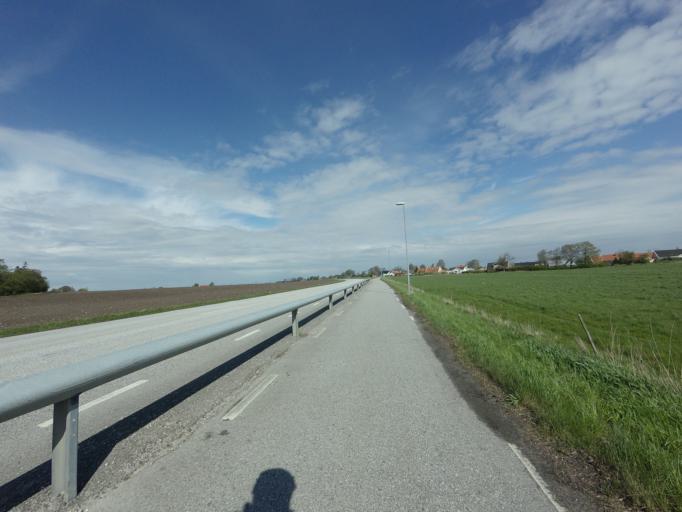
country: SE
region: Skane
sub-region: Vellinge Kommun
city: Vellinge
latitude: 55.4851
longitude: 13.0125
